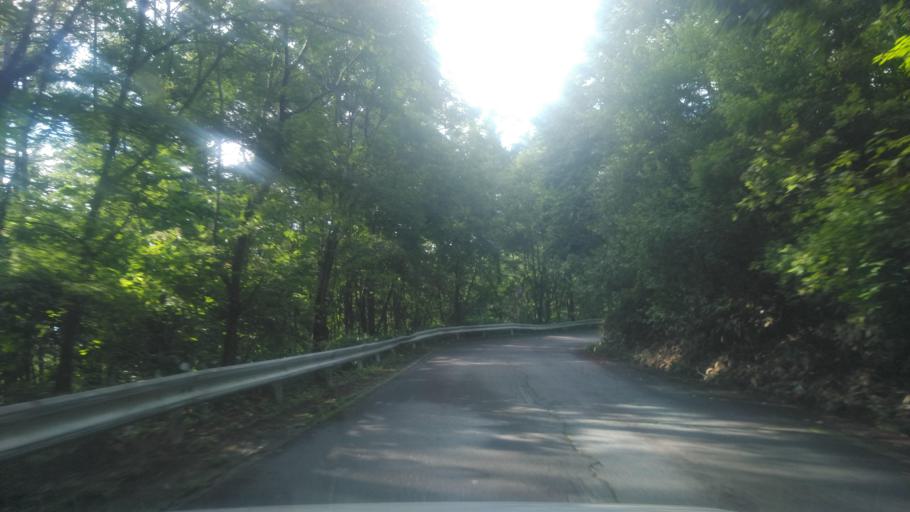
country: JP
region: Nagano
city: Ueda
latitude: 36.5063
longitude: 138.3750
